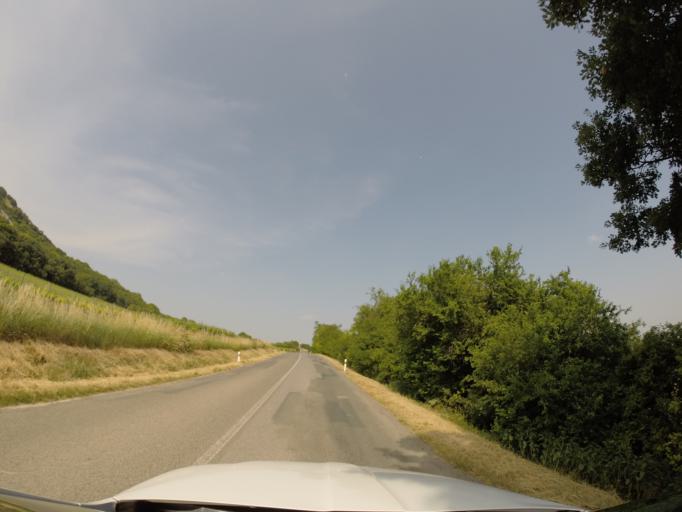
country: CZ
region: South Moravian
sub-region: Okres Breclav
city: Mikulov
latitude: 48.8635
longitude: 16.6555
